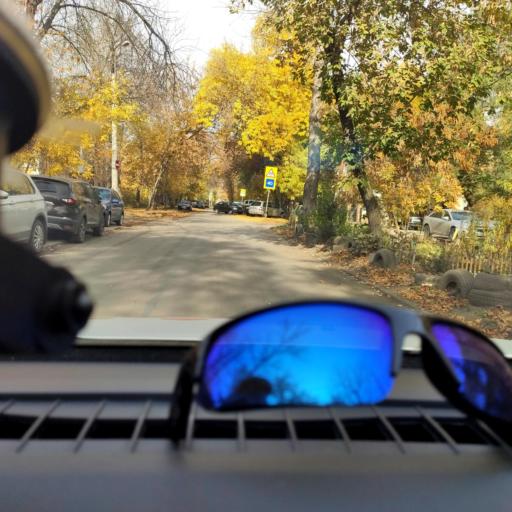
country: RU
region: Samara
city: Samara
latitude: 53.1171
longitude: 50.0795
